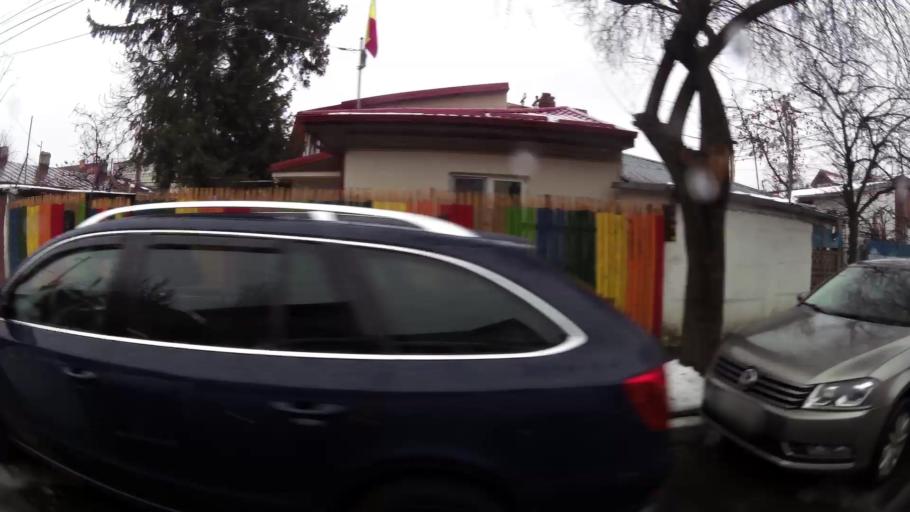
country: RO
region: Ilfov
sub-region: Comuna Chiajna
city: Rosu
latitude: 44.4927
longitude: 26.0429
